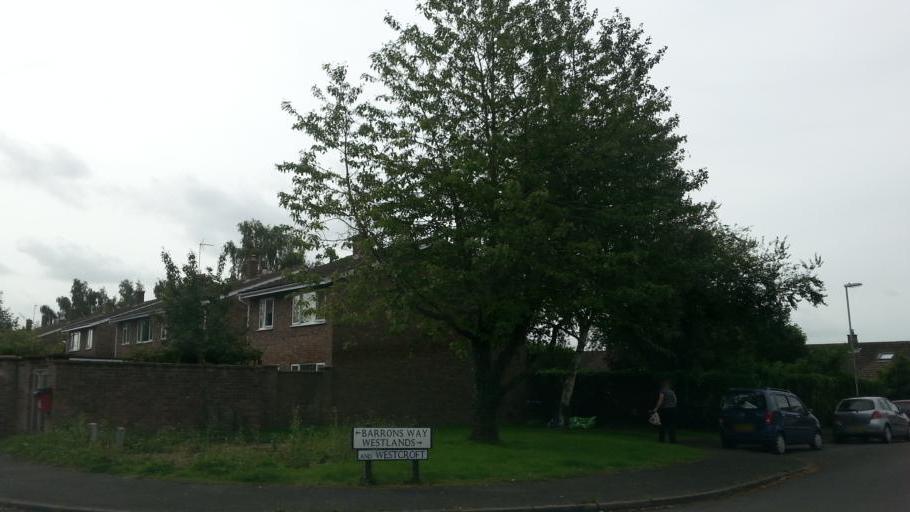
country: GB
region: England
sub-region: Cambridgeshire
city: Comberton
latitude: 52.1860
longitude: 0.0165
